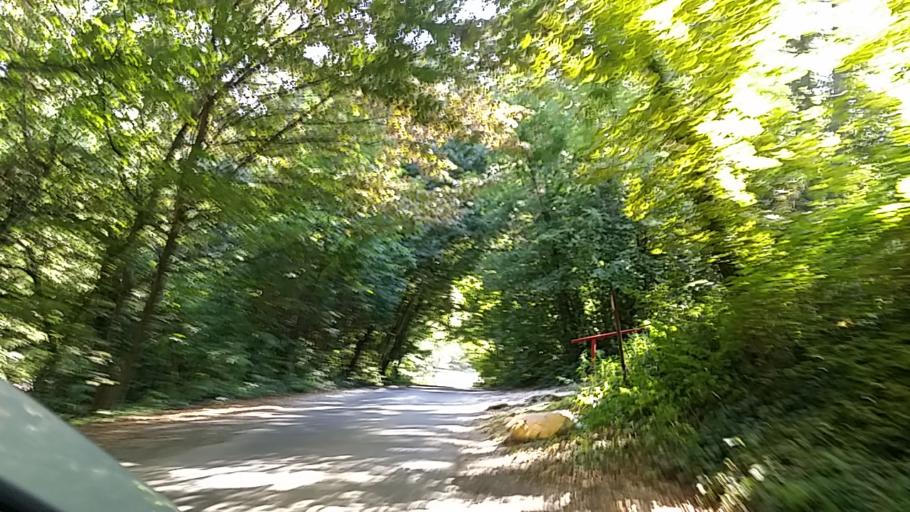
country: HU
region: Pest
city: Kismaros
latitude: 47.8395
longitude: 19.0062
